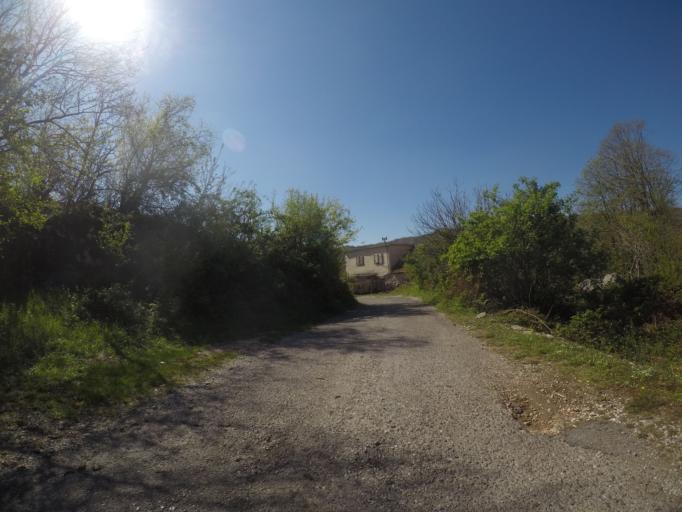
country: ME
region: Danilovgrad
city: Danilovgrad
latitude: 42.5213
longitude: 19.0506
